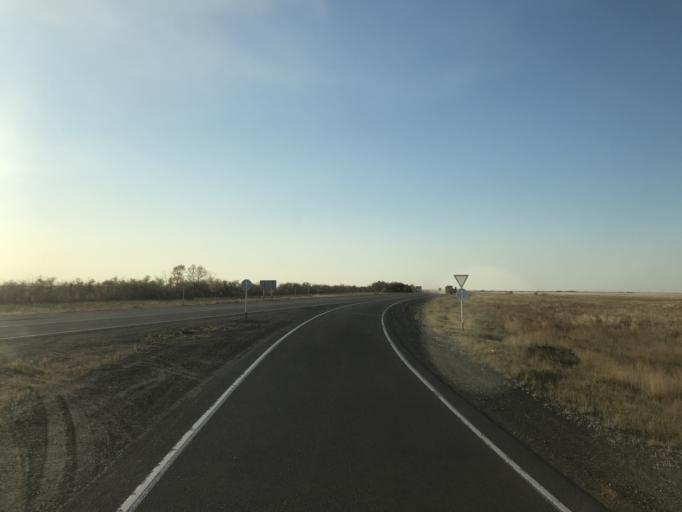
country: KZ
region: Pavlodar
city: Leninskiy
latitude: 52.1555
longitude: 76.8188
